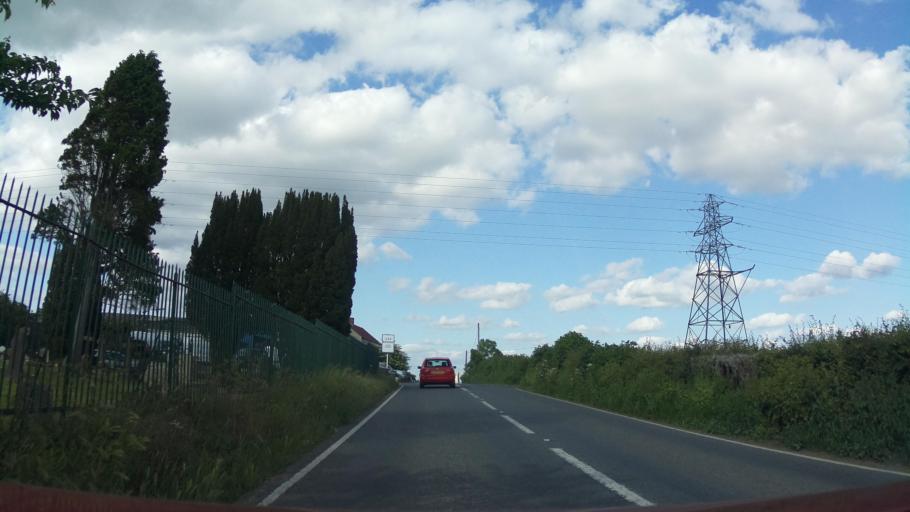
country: GB
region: England
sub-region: Somerset
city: Westonzoyland
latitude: 51.0768
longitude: -2.8907
